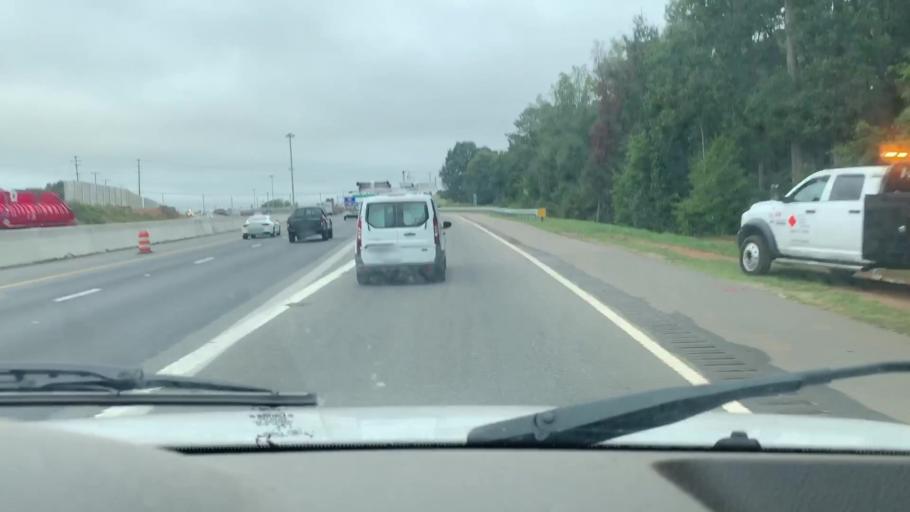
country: US
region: North Carolina
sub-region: Iredell County
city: Mooresville
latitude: 35.5753
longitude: -80.8556
